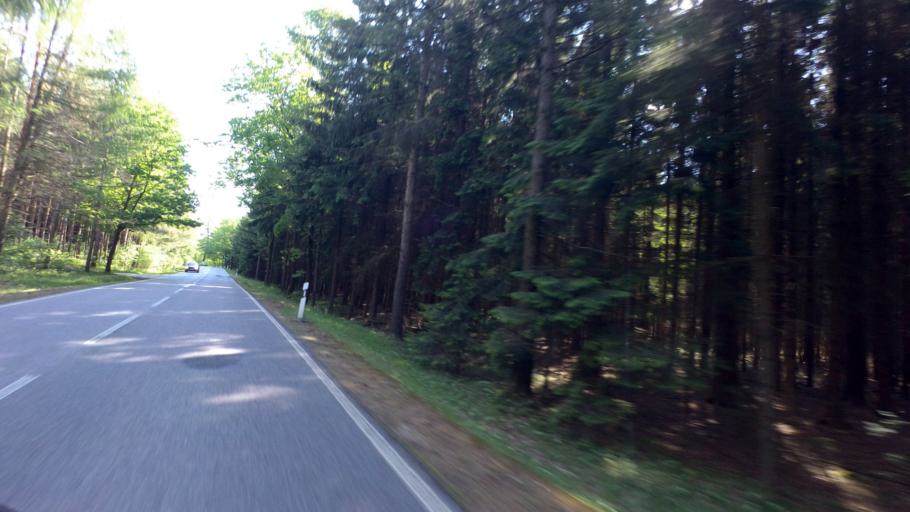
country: DE
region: Saxony
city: Hohnstein
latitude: 51.0187
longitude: 14.1092
